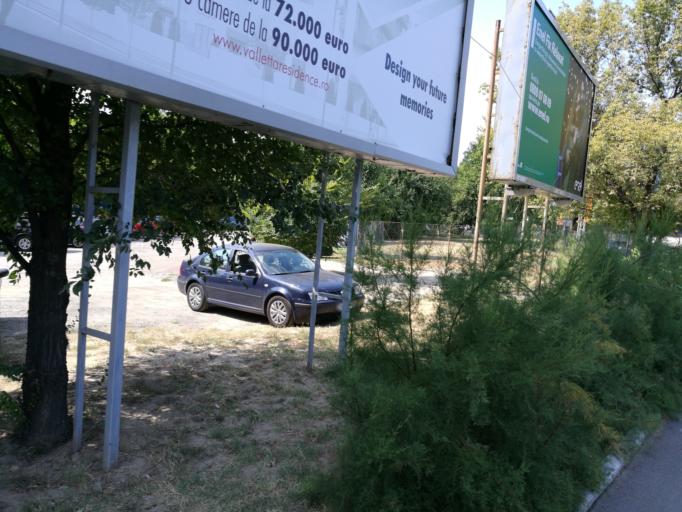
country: RO
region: Bucuresti
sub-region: Municipiul Bucuresti
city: Bucharest
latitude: 44.4747
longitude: 26.0910
